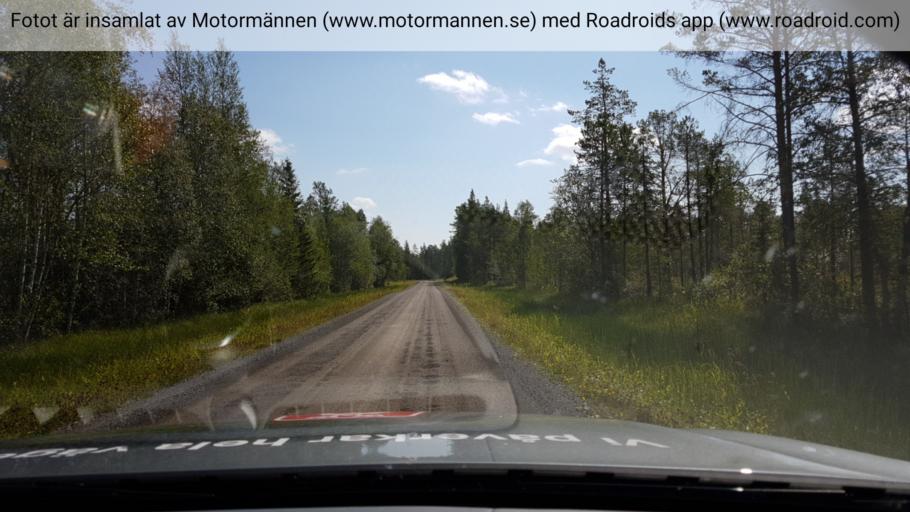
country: SE
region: Jaemtland
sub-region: OEstersunds Kommun
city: Lit
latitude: 63.3507
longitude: 15.3435
